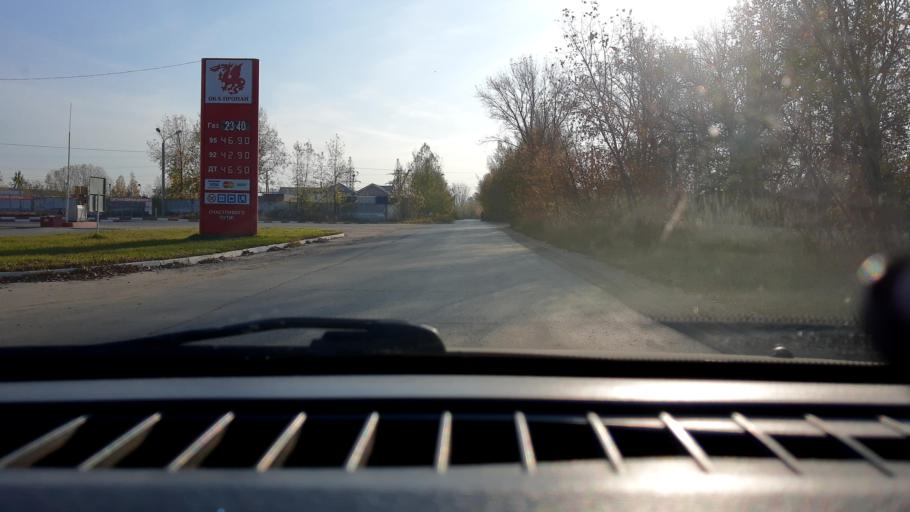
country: RU
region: Nizjnij Novgorod
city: Gorbatovka
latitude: 56.3741
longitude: 43.7920
